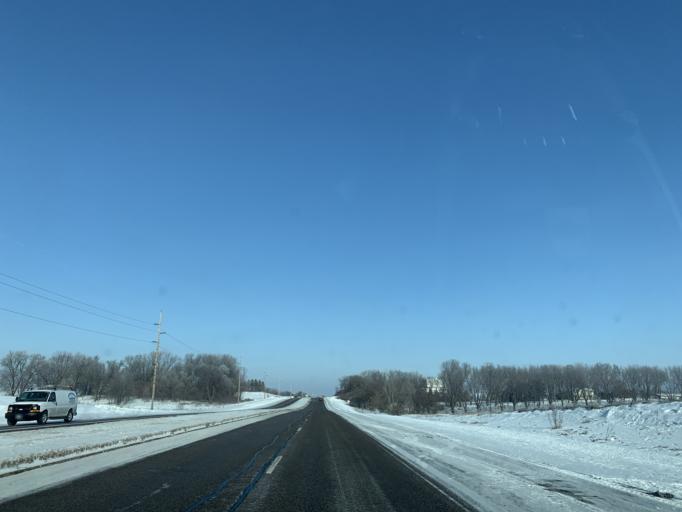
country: US
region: Minnesota
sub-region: Dakota County
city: Lakeville
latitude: 44.6662
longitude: -93.2174
